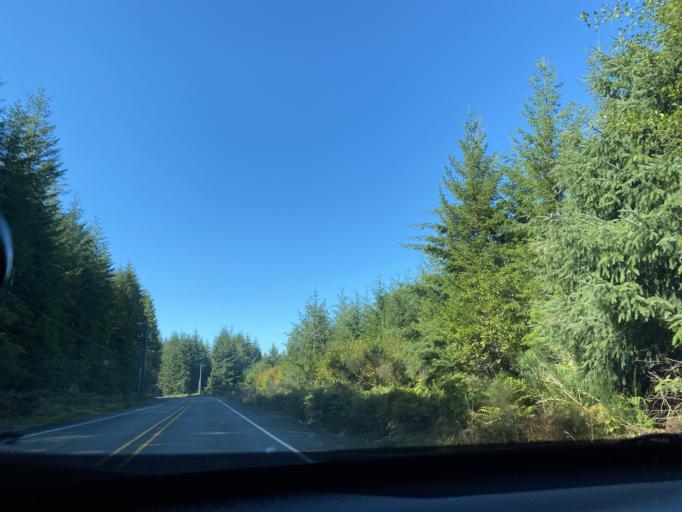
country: US
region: Washington
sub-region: Clallam County
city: Forks
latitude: 47.9537
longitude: -124.4570
